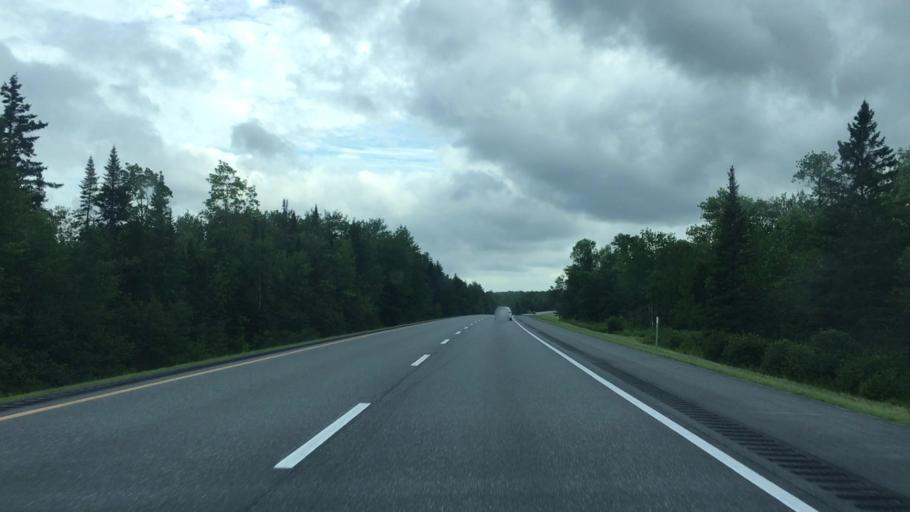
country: US
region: Maine
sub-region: Waldo County
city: Burnham
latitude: 44.7133
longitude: -69.4487
